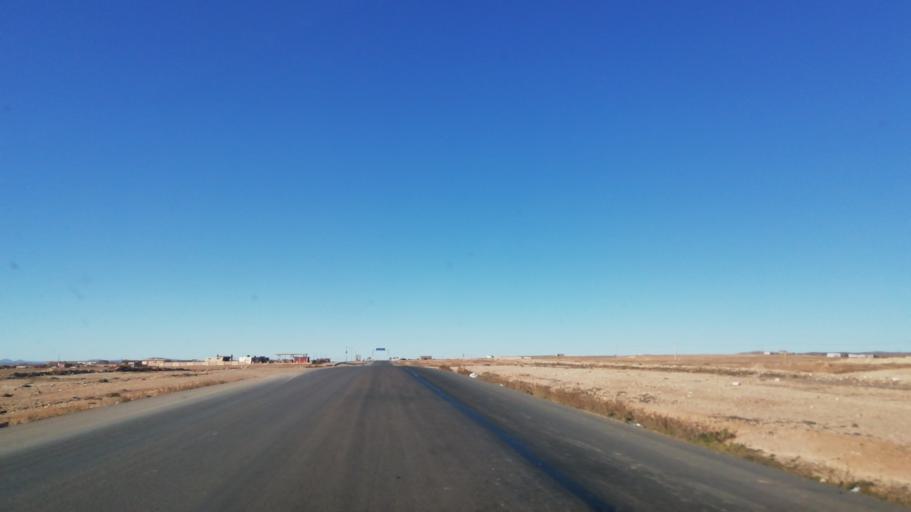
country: DZ
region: Tlemcen
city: Sebdou
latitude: 34.2064
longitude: -1.2393
